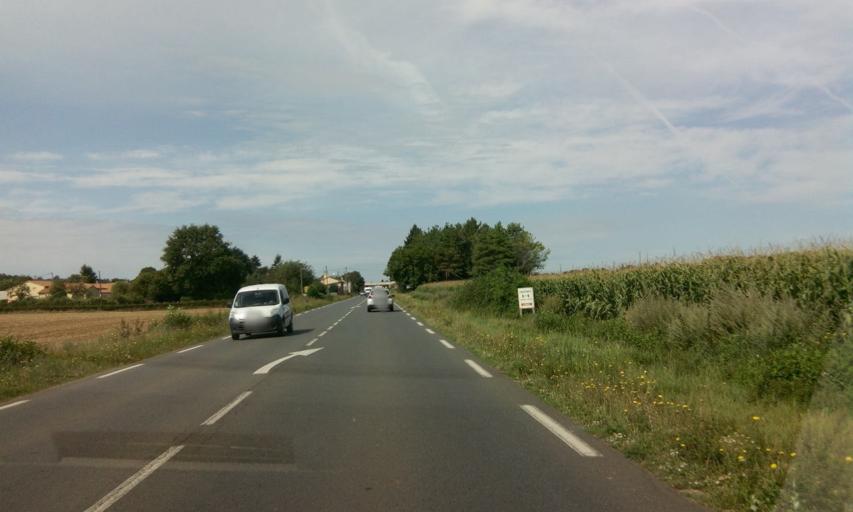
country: FR
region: Poitou-Charentes
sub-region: Departement des Deux-Sevres
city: Sauze-Vaussais
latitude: 46.1356
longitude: 0.1426
